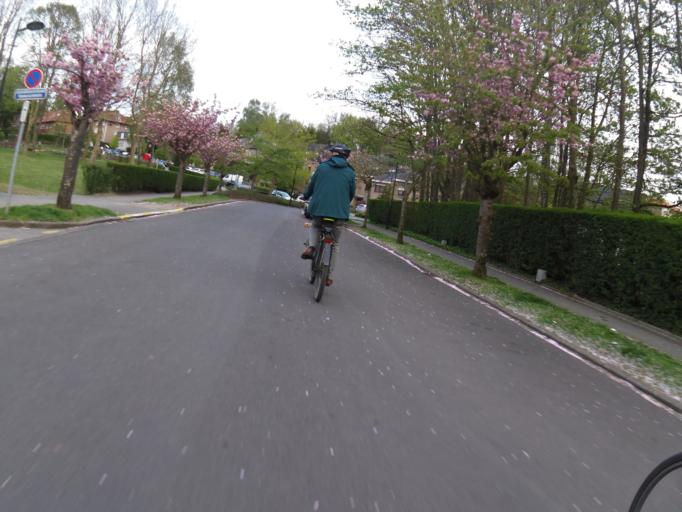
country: BE
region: Flanders
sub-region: Provincie Vlaams-Brabant
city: Kraainem
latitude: 50.8244
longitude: 4.4549
